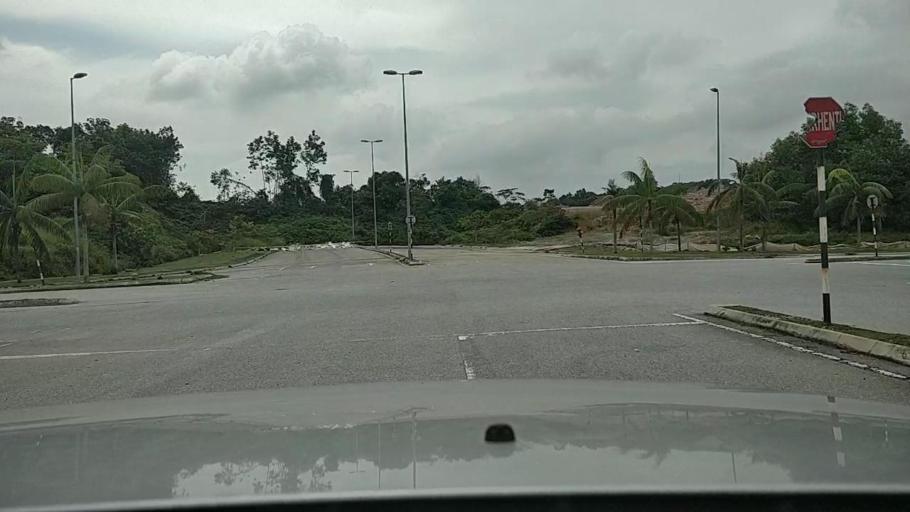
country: MY
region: Putrajaya
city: Putrajaya
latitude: 2.8975
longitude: 101.6454
